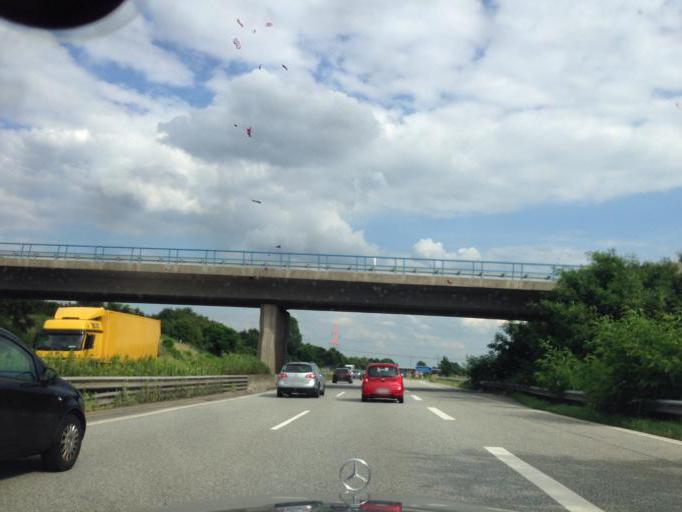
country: DE
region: Schleswig-Holstein
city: Oststeinbek
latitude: 53.4812
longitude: 10.1485
